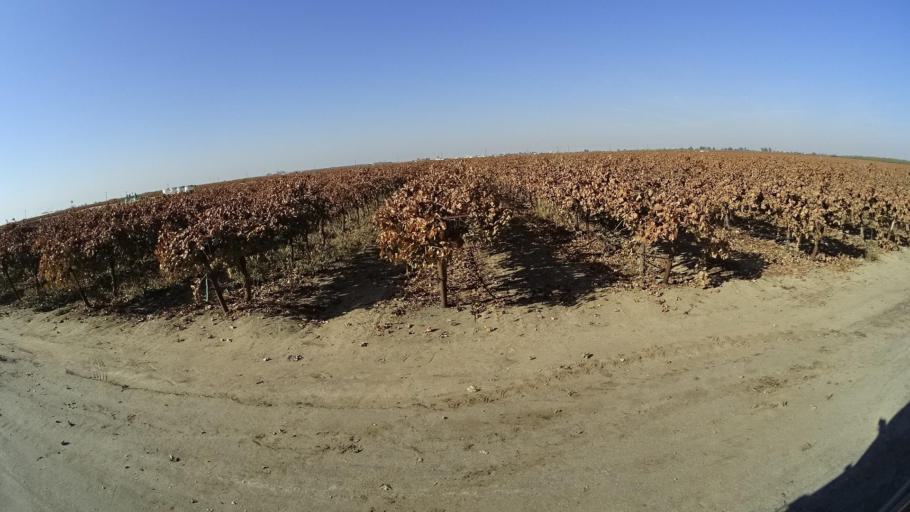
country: US
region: California
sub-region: Kern County
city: Delano
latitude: 35.7426
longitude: -119.2142
